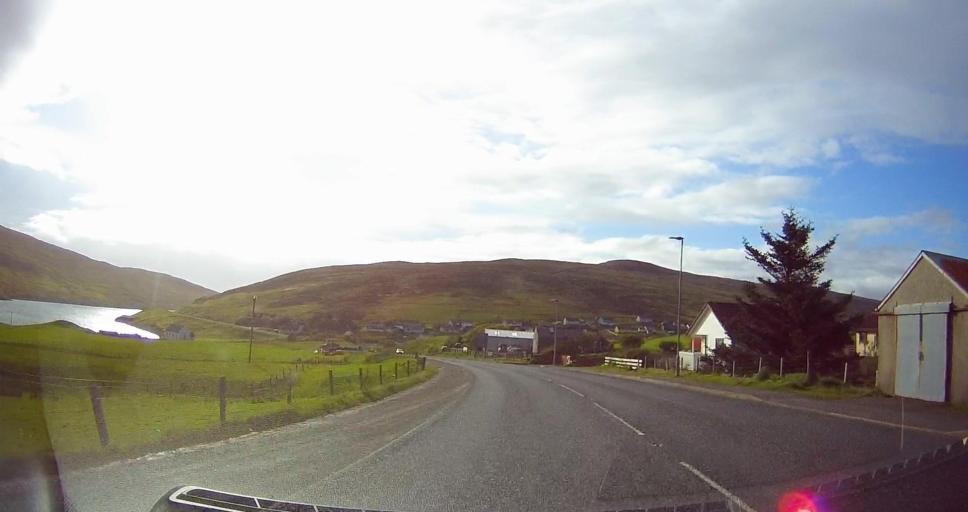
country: GB
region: Scotland
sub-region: Shetland Islands
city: Lerwick
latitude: 60.3555
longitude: -1.2624
